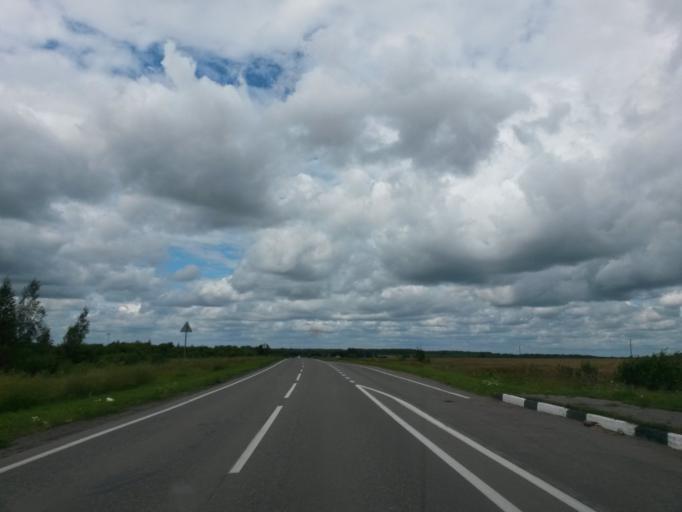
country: RU
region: Jaroslavl
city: Konstantinovskiy
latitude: 57.8705
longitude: 39.5968
